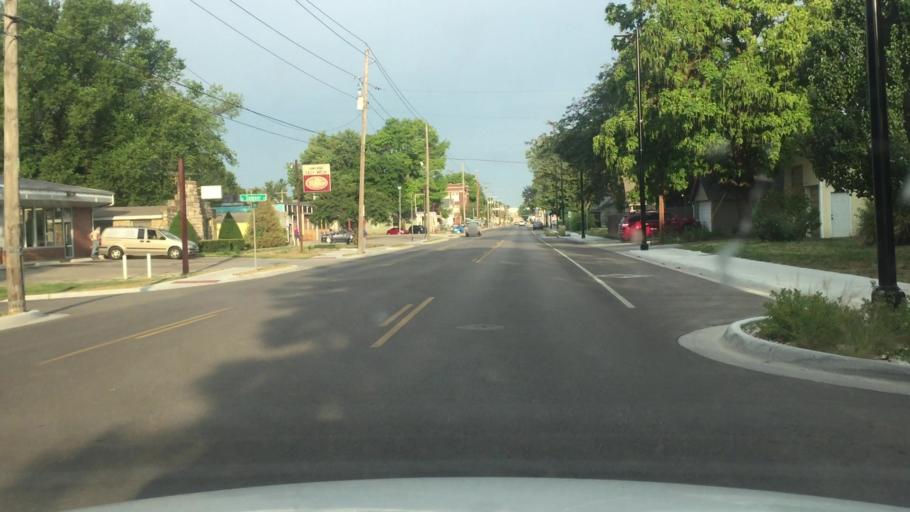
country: US
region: Kansas
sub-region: Shawnee County
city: Topeka
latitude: 39.0589
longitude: -95.6442
